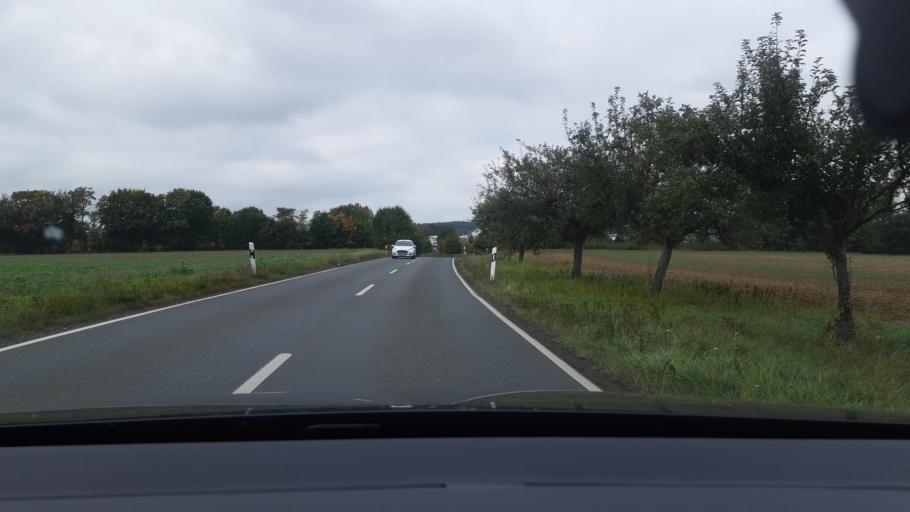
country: DE
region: Hesse
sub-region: Regierungsbezirk Giessen
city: Hoernsheim
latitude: 50.5230
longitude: 8.5967
